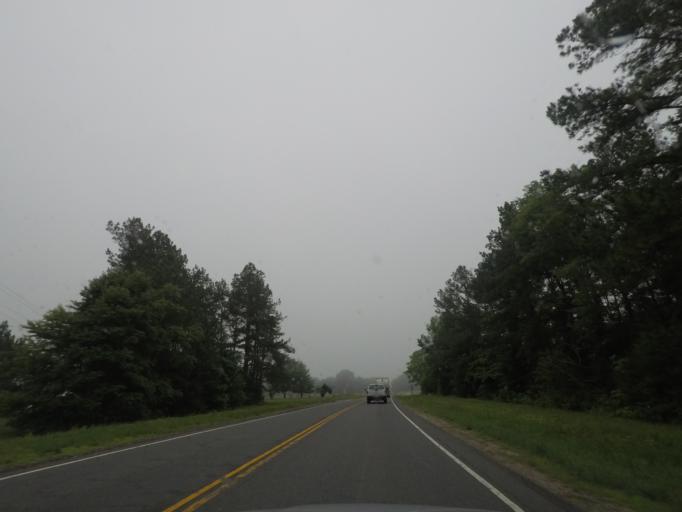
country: US
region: Virginia
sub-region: Buckingham County
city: Buckingham
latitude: 37.5104
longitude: -78.4893
